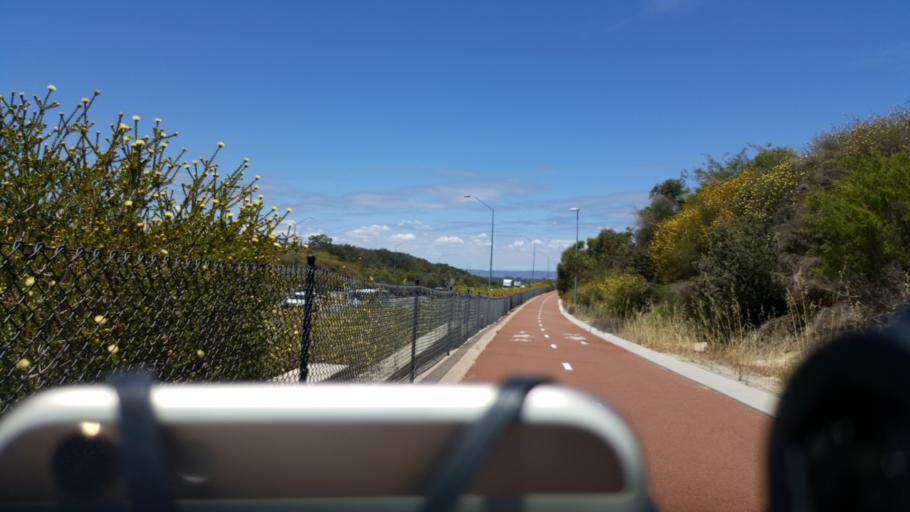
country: AU
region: Western Australia
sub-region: Stirling
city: Westminster
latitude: -31.8667
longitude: 115.8675
